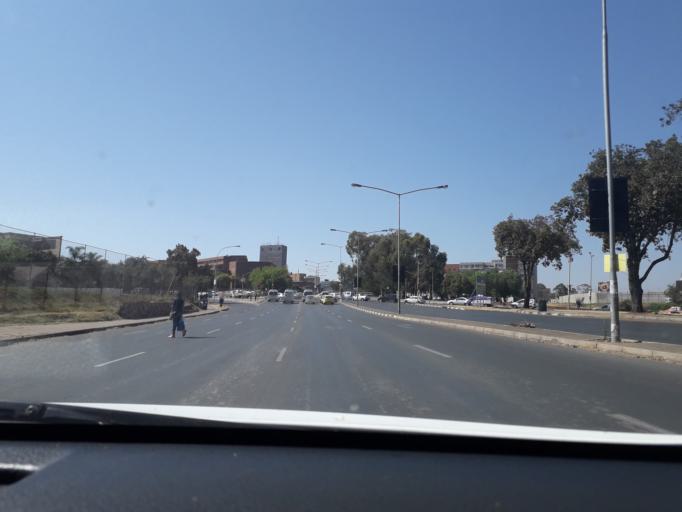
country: ZA
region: Gauteng
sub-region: City of Johannesburg Metropolitan Municipality
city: Modderfontein
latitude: -26.1000
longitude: 28.2243
